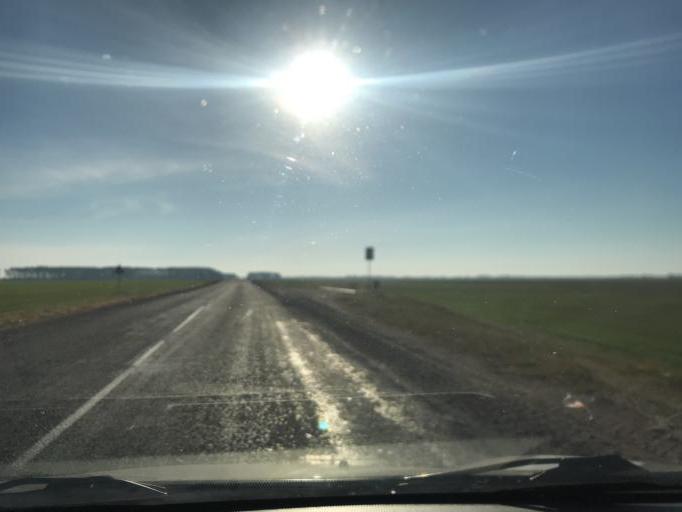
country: BY
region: Gomel
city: Khoyniki
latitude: 51.8243
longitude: 30.0726
